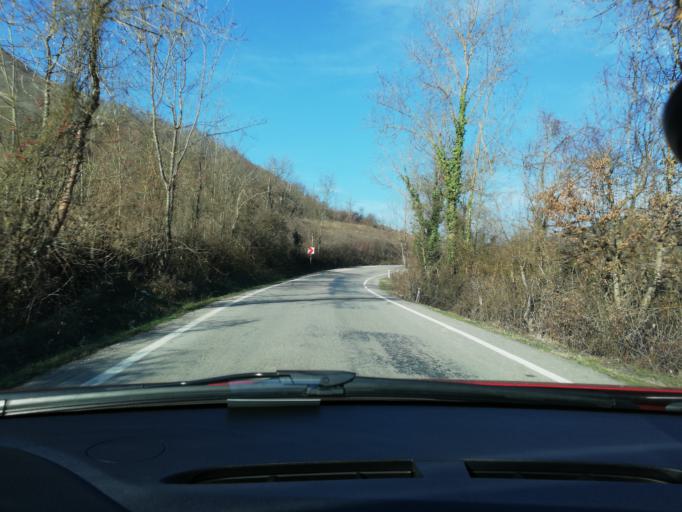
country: TR
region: Bartin
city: Kumluca
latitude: 41.4564
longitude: 32.5174
